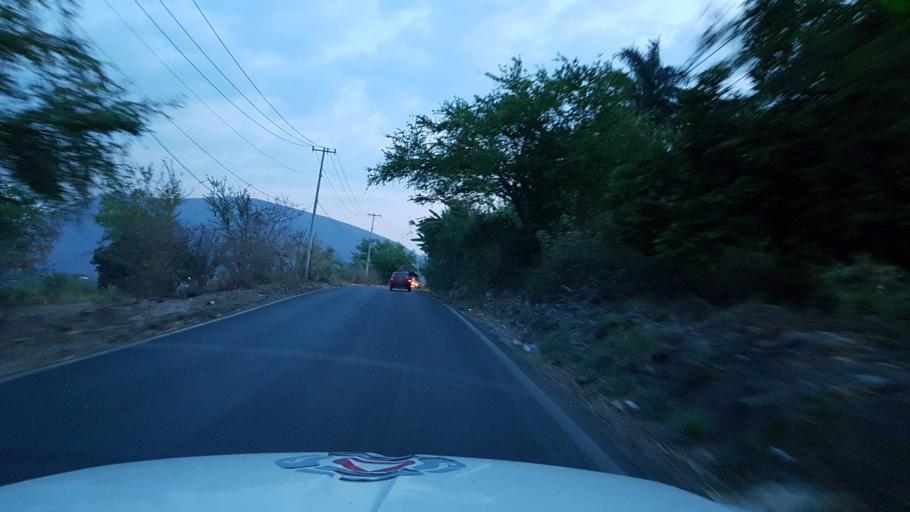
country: MX
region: Morelos
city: Tlaltizapan
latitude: 18.6911
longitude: -99.1325
